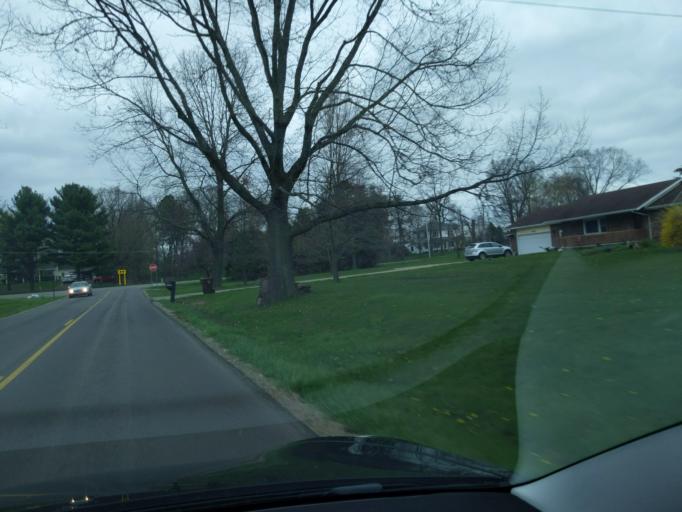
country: US
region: Michigan
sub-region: Ingham County
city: Stockbridge
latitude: 42.4529
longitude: -84.1506
